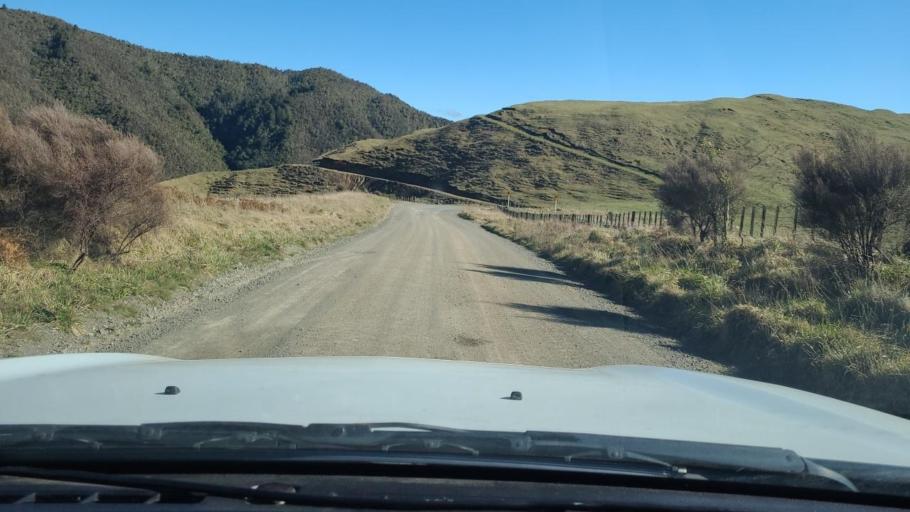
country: NZ
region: Hawke's Bay
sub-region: Napier City
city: Taradale
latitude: -39.2387
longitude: 176.4961
